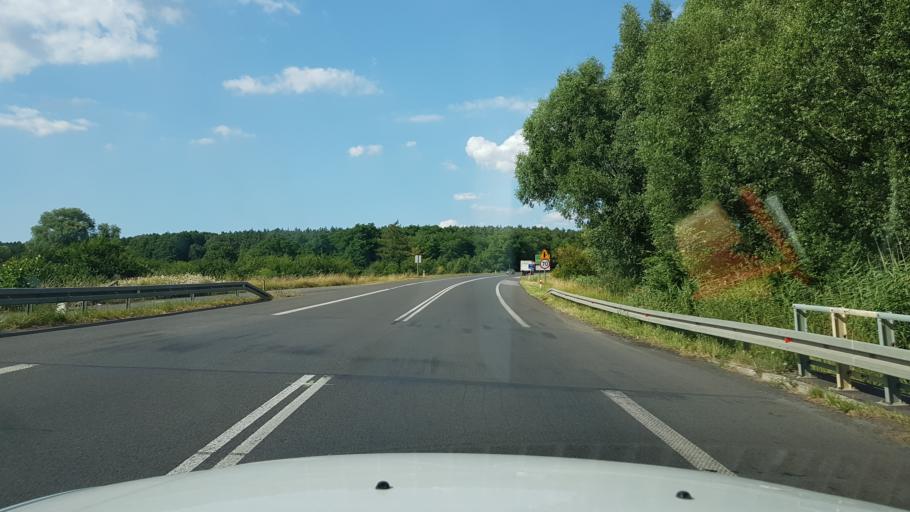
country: PL
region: West Pomeranian Voivodeship
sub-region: Powiat gryfinski
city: Stare Czarnowo
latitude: 53.2483
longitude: 14.7805
